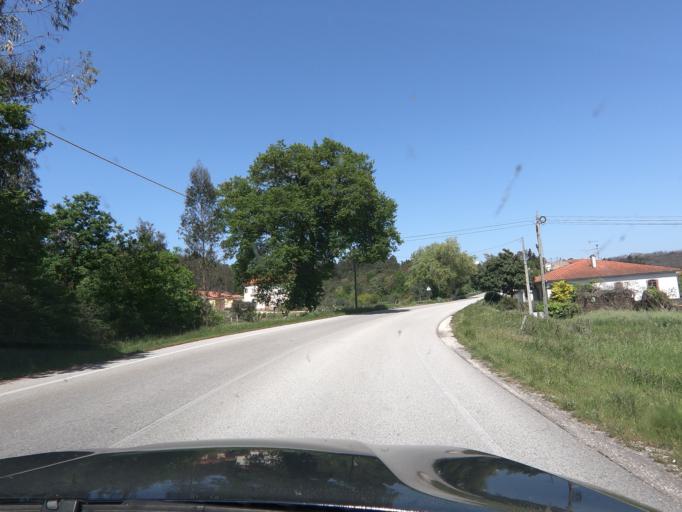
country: PT
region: Coimbra
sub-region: Vila Nova de Poiares
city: Poiares
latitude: 40.1876
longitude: -8.2558
